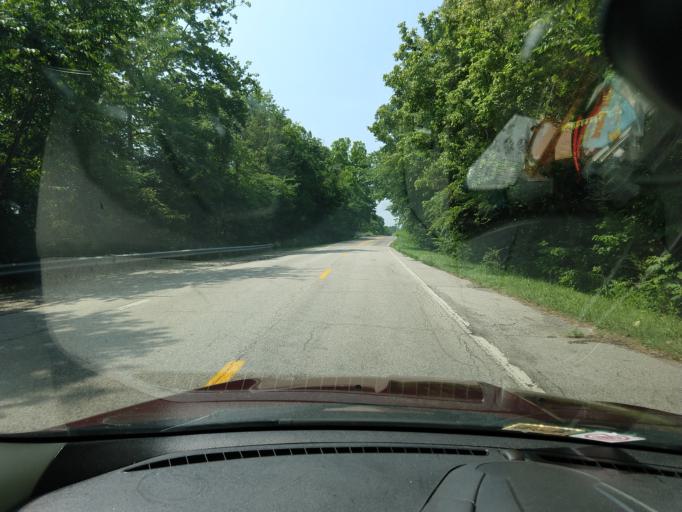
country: US
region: West Virginia
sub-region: Mason County
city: New Haven
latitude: 38.9213
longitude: -81.9143
